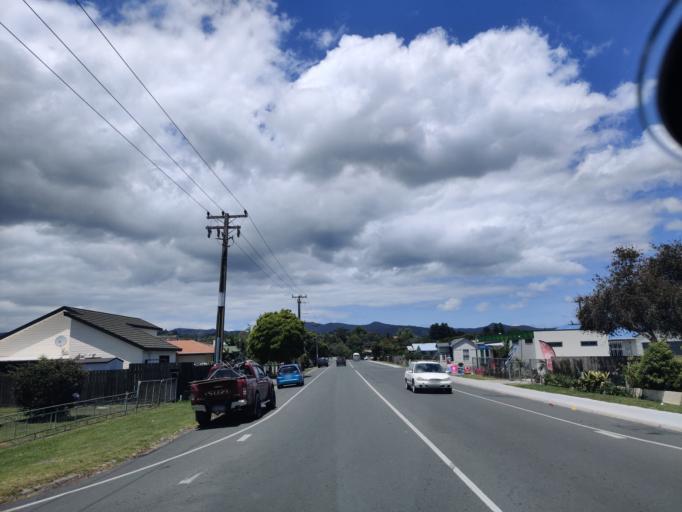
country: NZ
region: Northland
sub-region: Far North District
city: Kaitaia
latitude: -35.1103
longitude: 173.2586
